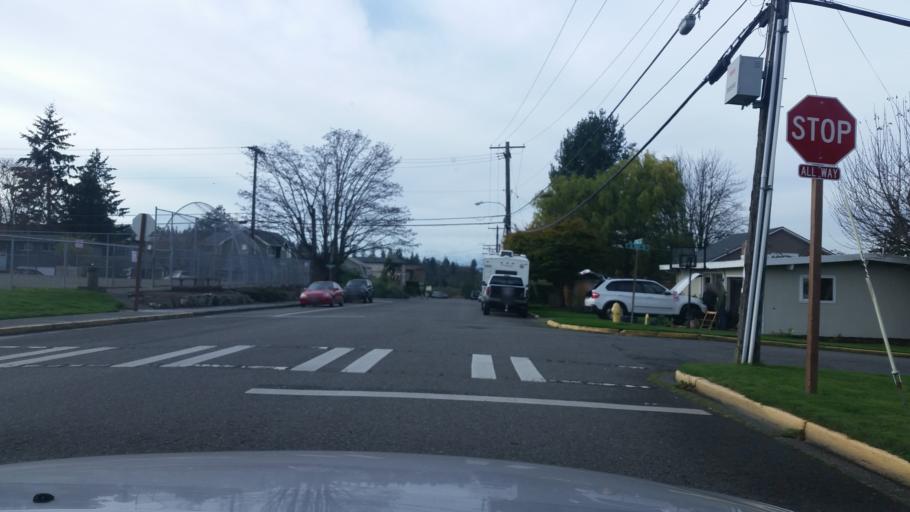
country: US
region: Washington
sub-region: Snohomish County
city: Edmonds
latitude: 47.8032
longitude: -122.3740
